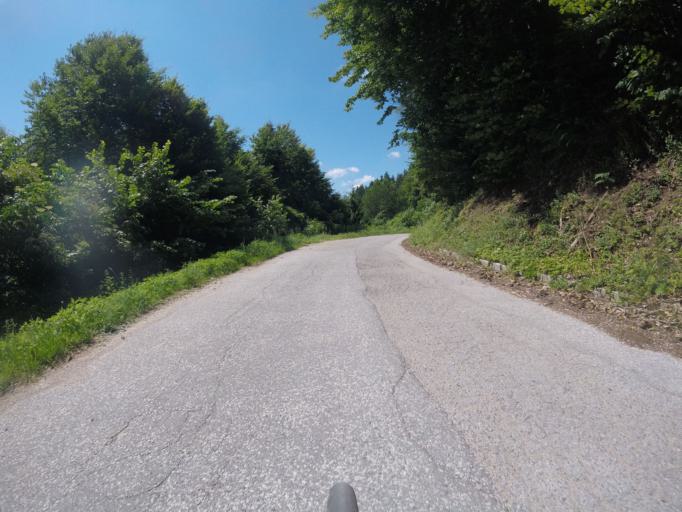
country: SI
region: Kostanjevica na Krki
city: Kostanjevica na Krki
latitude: 45.7836
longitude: 15.4795
